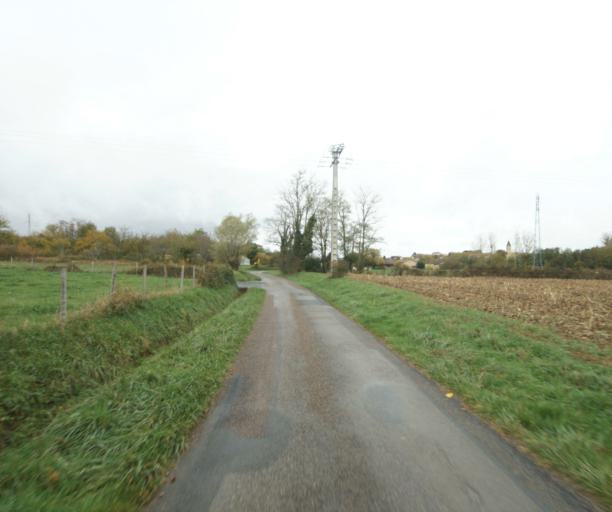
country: FR
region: Rhone-Alpes
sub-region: Departement de l'Ain
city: Pont-de-Vaux
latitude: 46.4732
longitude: 4.8797
